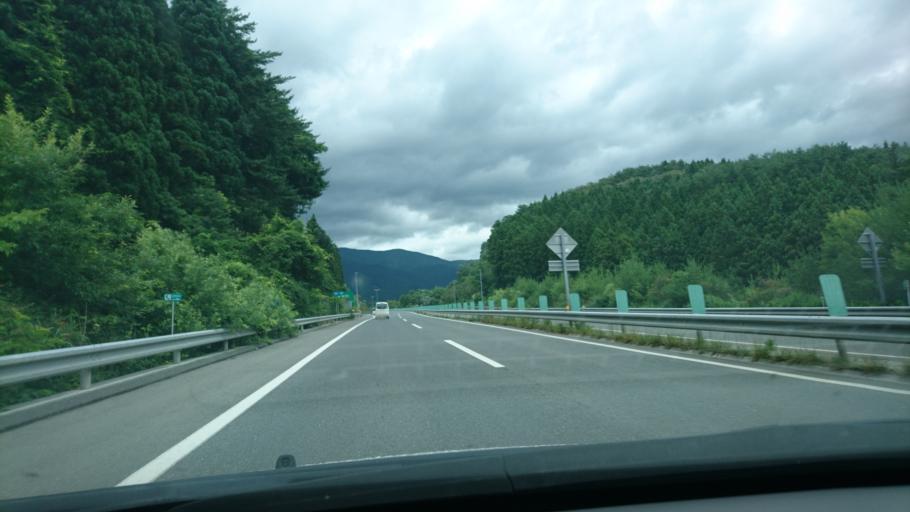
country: JP
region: Iwate
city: Ofunato
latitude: 39.1035
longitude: 141.7056
